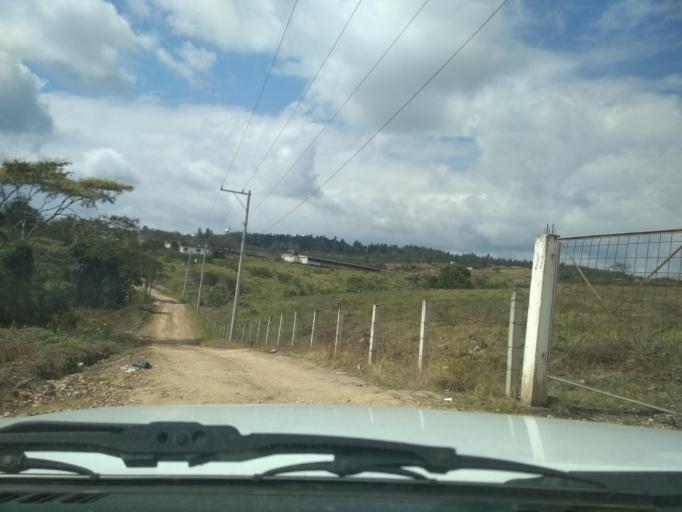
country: MX
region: Veracruz
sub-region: Emiliano Zapata
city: Jacarandas
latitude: 19.5031
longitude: -96.8263
